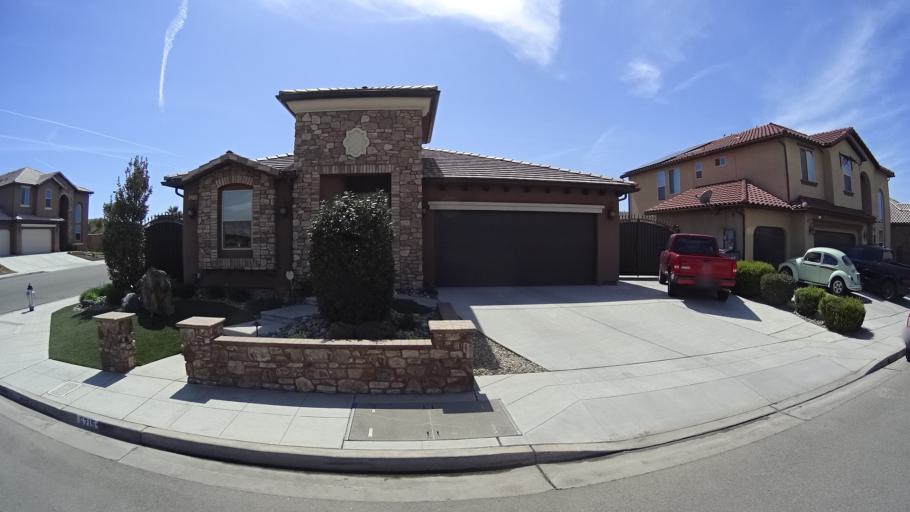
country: US
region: California
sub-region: Fresno County
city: Biola
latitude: 36.8229
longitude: -119.9112
